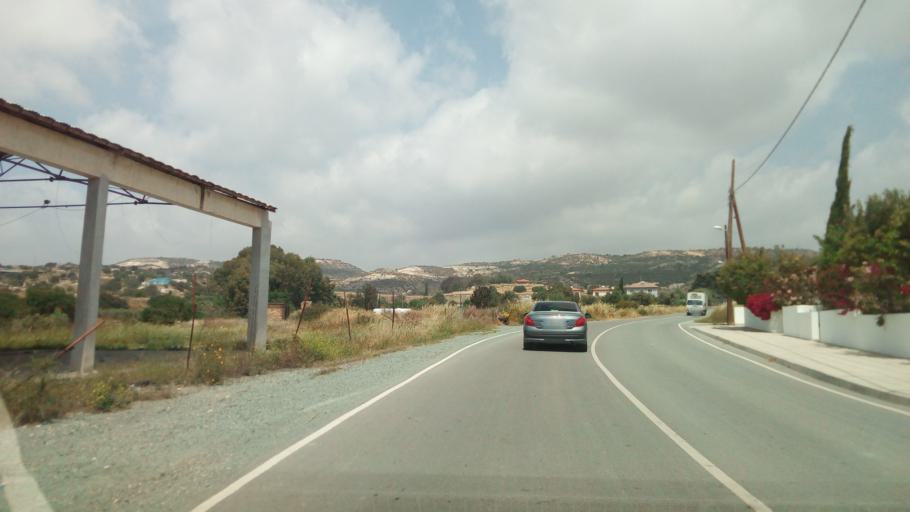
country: CY
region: Limassol
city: Pissouri
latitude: 34.6728
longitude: 32.7212
